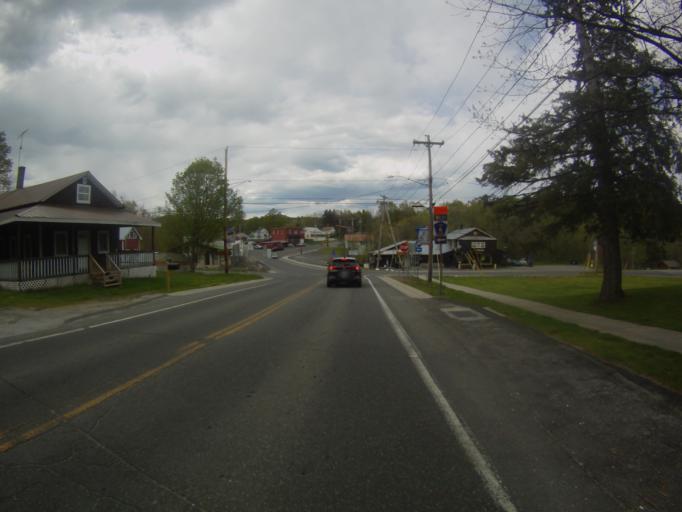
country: US
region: New York
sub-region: Essex County
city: Mineville
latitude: 44.0607
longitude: -73.5096
